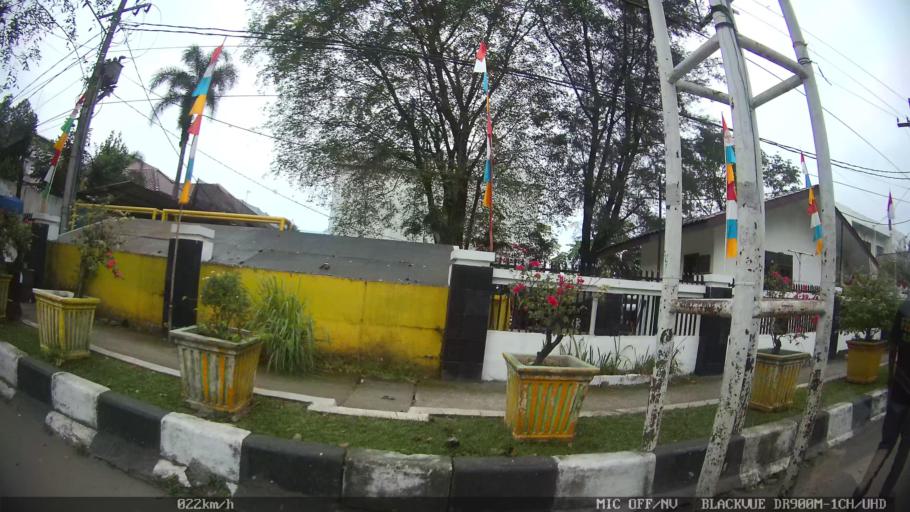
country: ID
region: North Sumatra
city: Medan
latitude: 3.5531
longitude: 98.6915
